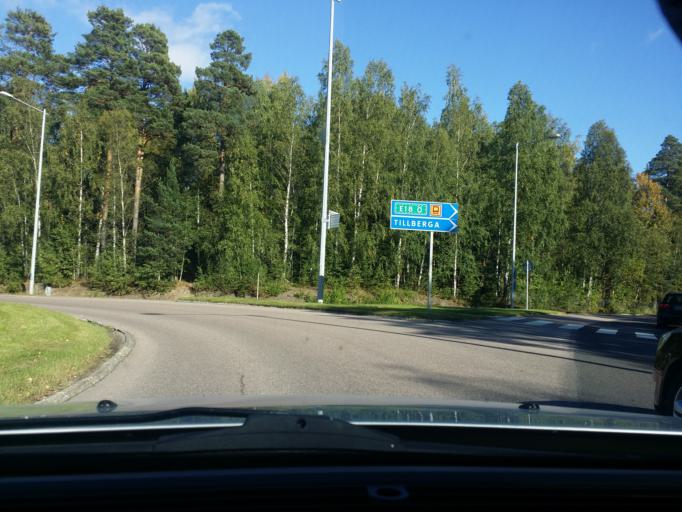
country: SE
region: Vaestmanland
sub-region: Vasteras
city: Vasteras
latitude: 59.6318
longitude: 16.5830
